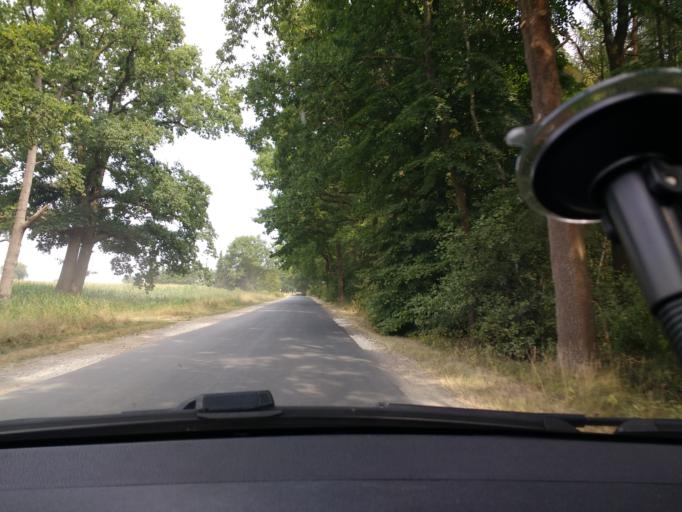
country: DE
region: Lower Saxony
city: Wagenhoff
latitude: 52.5218
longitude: 10.5558
